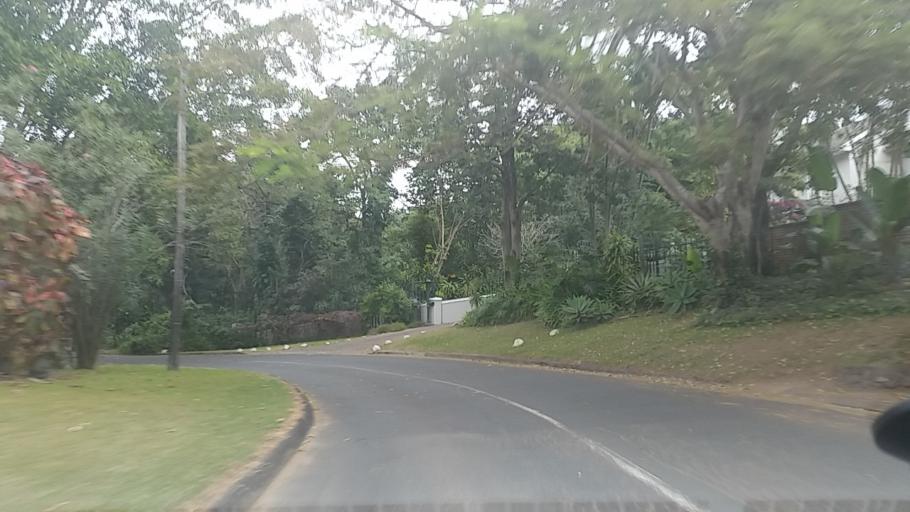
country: ZA
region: KwaZulu-Natal
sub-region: eThekwini Metropolitan Municipality
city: Berea
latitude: -29.8401
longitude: 30.9303
